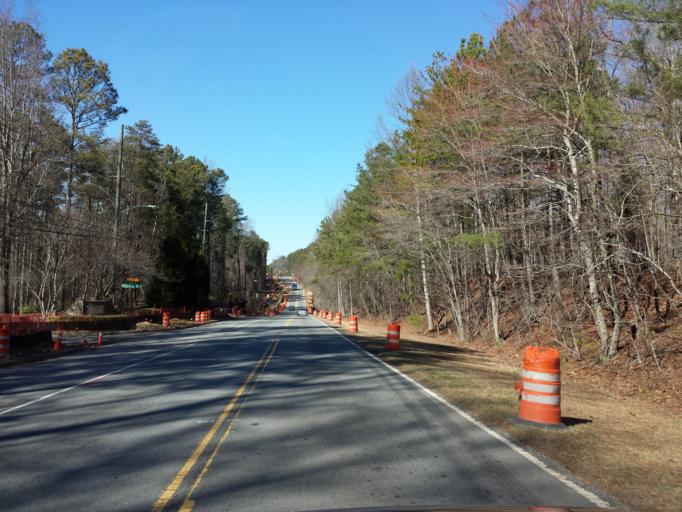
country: US
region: Georgia
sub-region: Cobb County
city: Marietta
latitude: 33.9397
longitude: -84.6053
